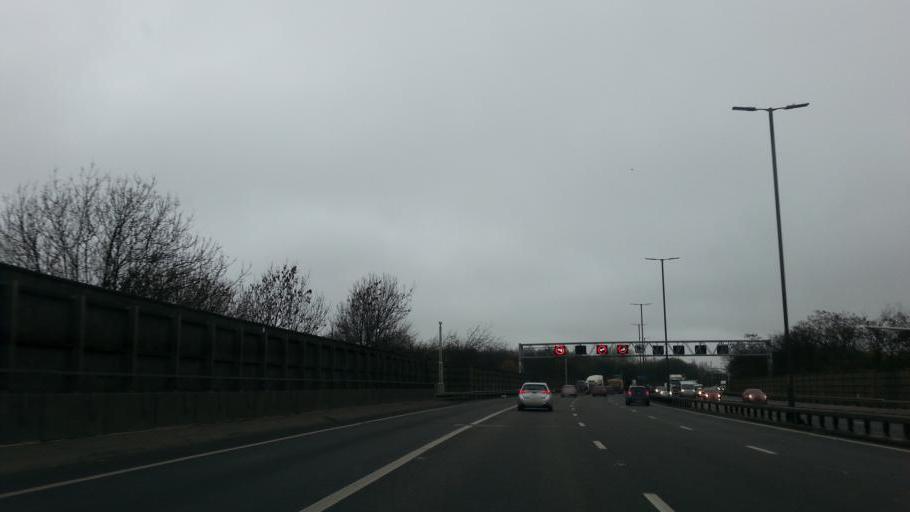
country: GB
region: England
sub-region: City and Borough of Birmingham
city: Hockley
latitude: 52.5284
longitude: -1.8960
